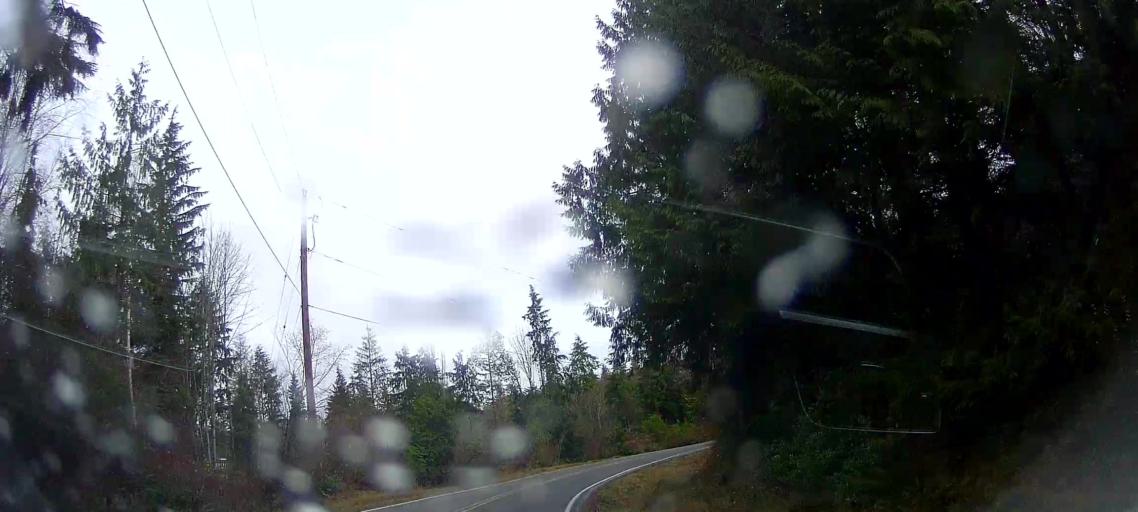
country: US
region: Washington
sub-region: Skagit County
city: Clear Lake
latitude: 48.4767
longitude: -122.1655
